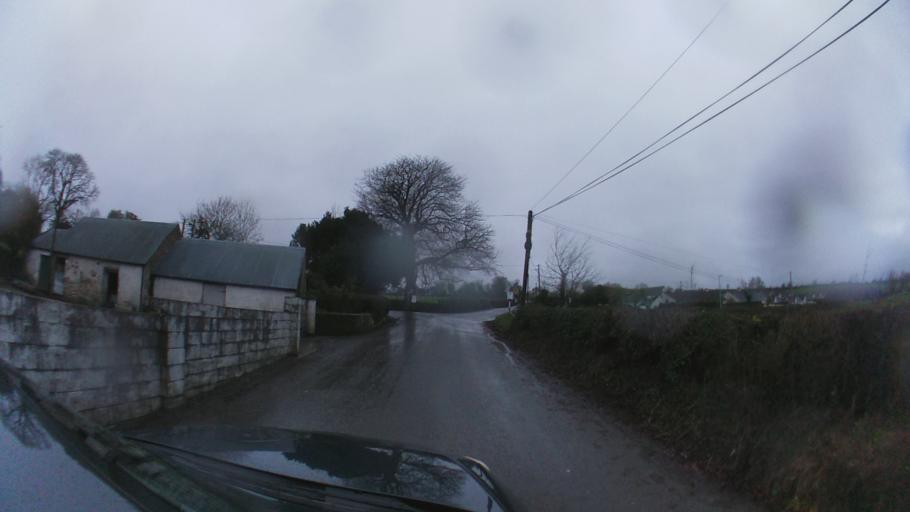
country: IE
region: Leinster
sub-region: Kilkenny
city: Graiguenamanagh
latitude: 52.5917
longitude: -6.9932
